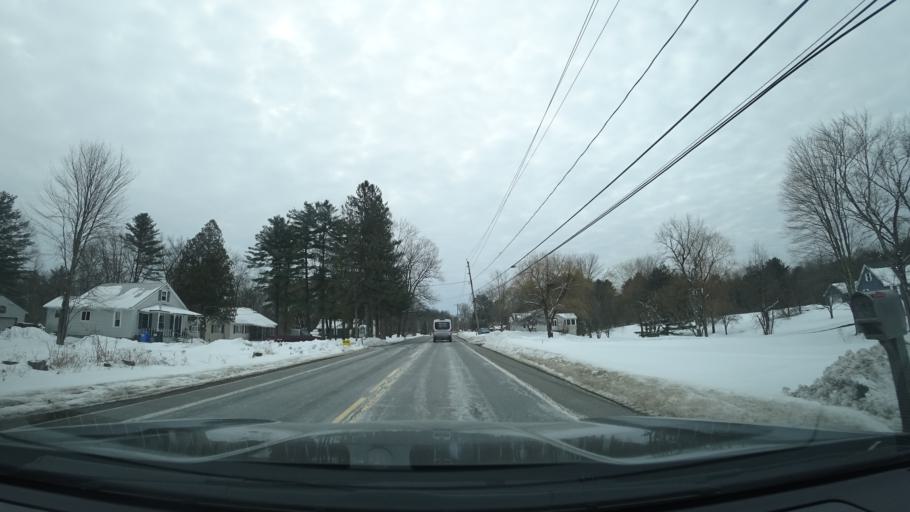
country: US
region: New York
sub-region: Washington County
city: Fort Edward
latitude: 43.2722
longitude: -73.6086
